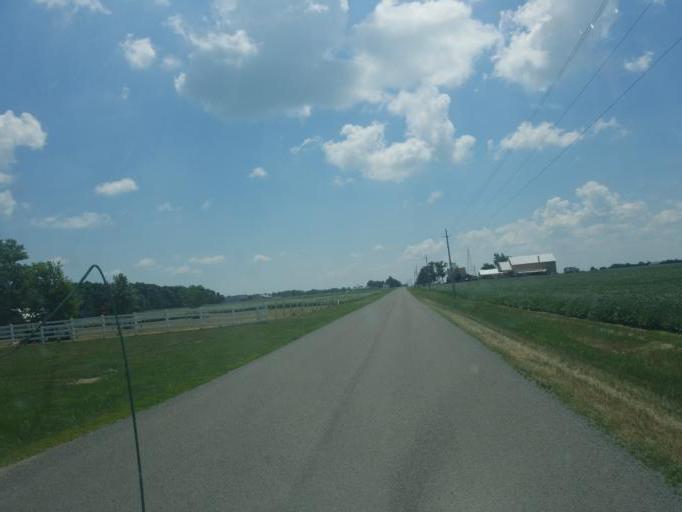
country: US
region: Ohio
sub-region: Mercer County
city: Celina
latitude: 40.5629
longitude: -84.4939
